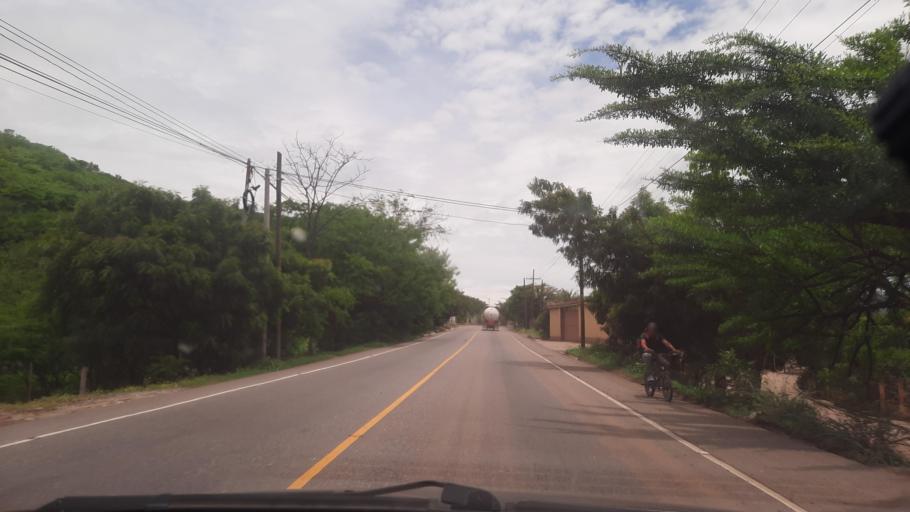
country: GT
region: Zacapa
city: Rio Hondo
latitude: 15.0782
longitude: -89.4909
